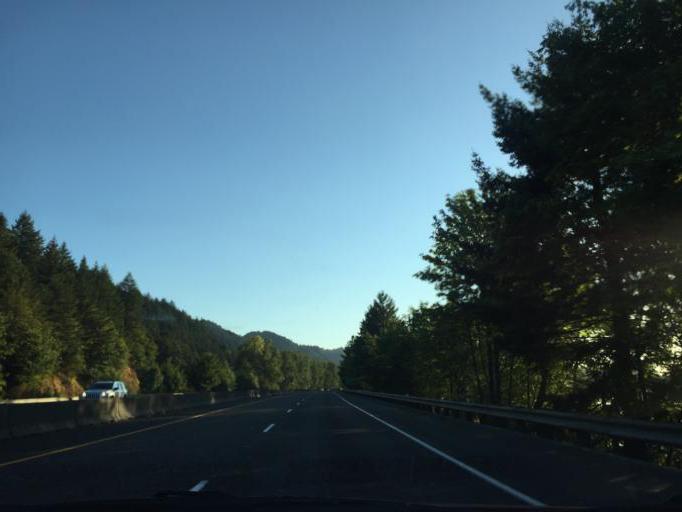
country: US
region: Washington
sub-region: Clark County
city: Washougal
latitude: 45.5534
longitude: -122.1886
